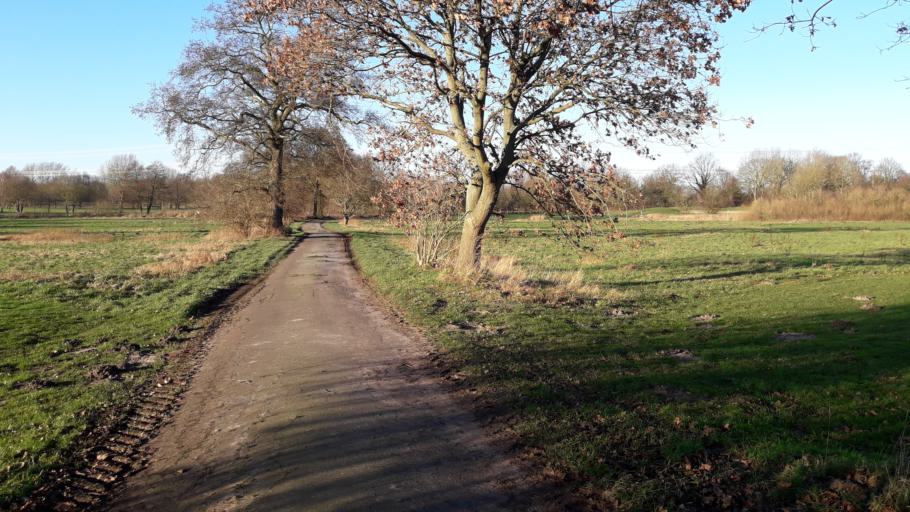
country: DE
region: Schleswig-Holstein
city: Quickborn
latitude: 53.7147
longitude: 9.8626
